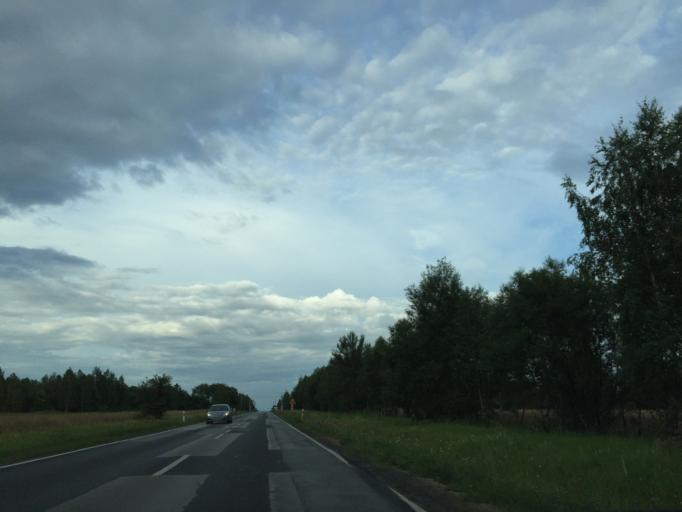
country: PL
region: Lublin Voivodeship
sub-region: Powiat lubartowski
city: Lubartow
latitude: 51.4345
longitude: 22.6089
